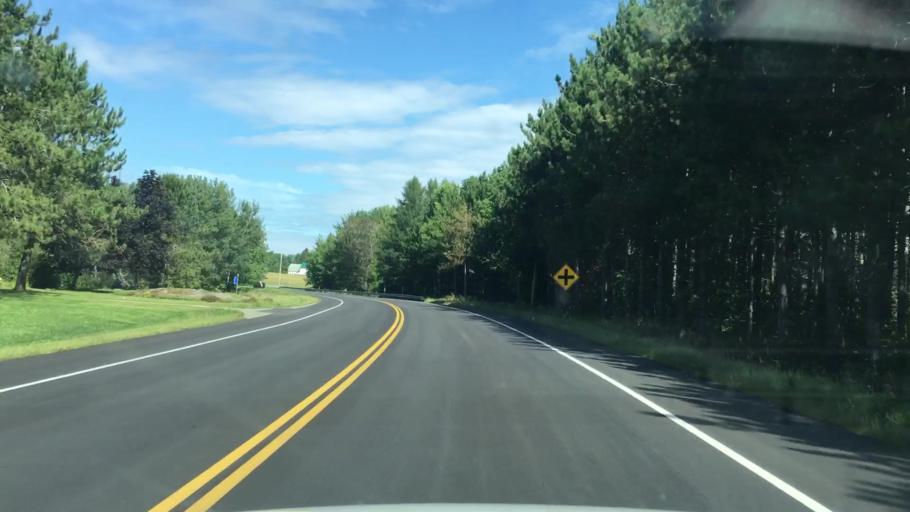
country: US
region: Maine
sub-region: Penobscot County
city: Corinna
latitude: 44.9463
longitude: -69.2463
